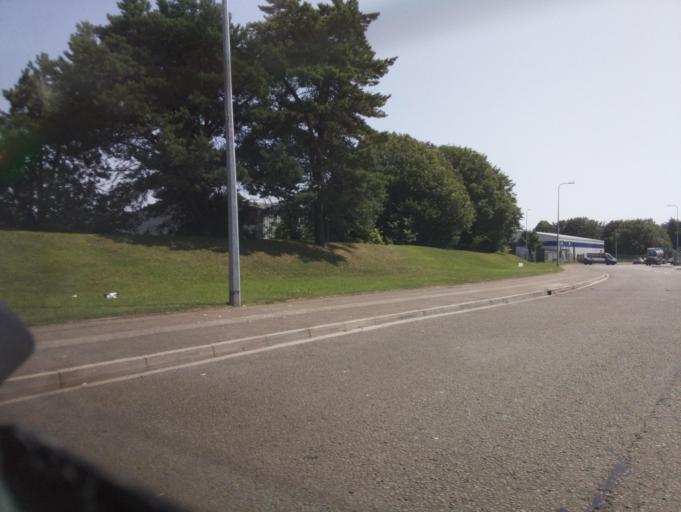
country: GB
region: Wales
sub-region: Cardiff
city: Cardiff
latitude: 51.4768
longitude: -3.1484
